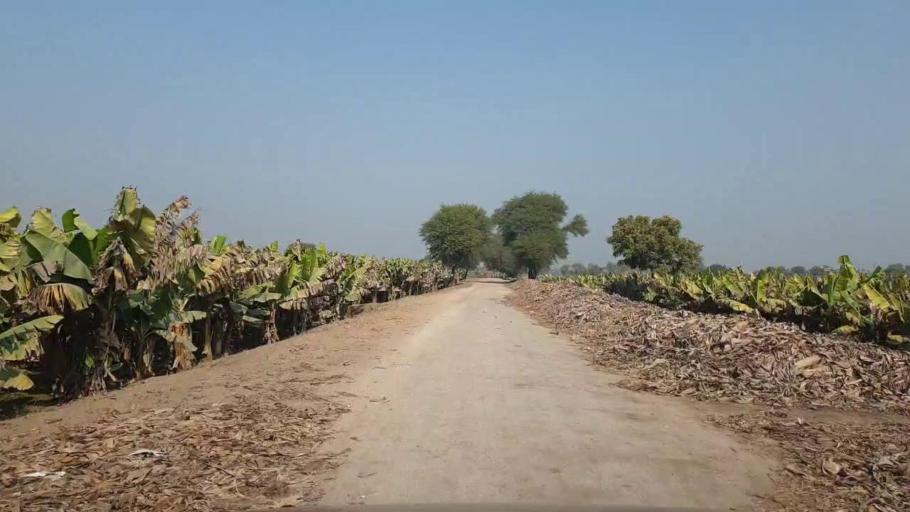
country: PK
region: Sindh
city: Bhit Shah
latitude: 25.7707
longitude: 68.5126
